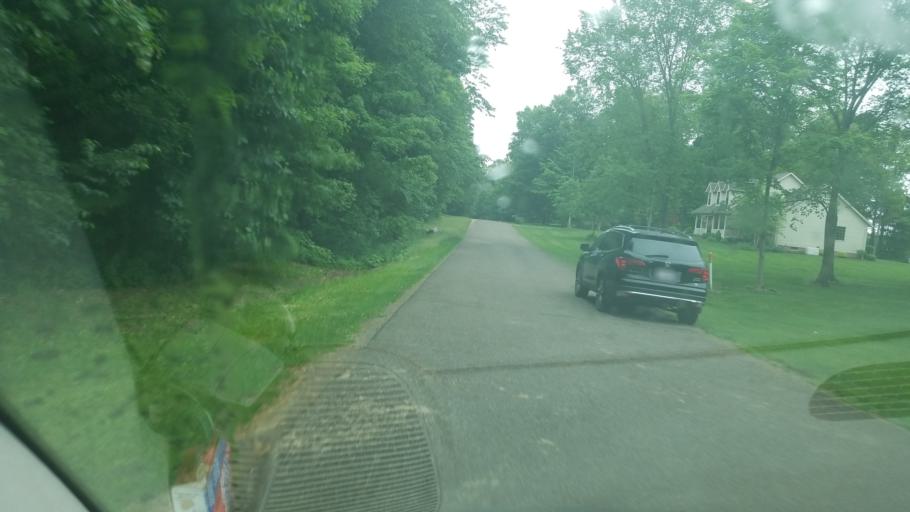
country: US
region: Ohio
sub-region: Knox County
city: Fredericktown
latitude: 40.4929
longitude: -82.5684
